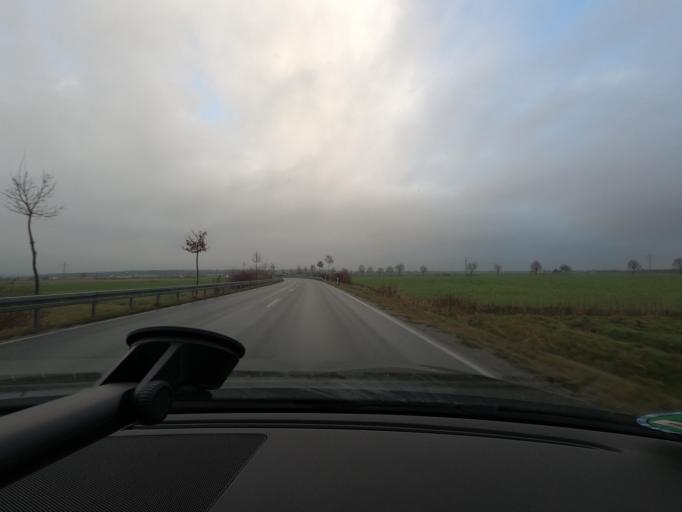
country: DE
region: North Rhine-Westphalia
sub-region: Regierungsbezirk Detmold
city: Buren
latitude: 51.5736
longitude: 8.5410
